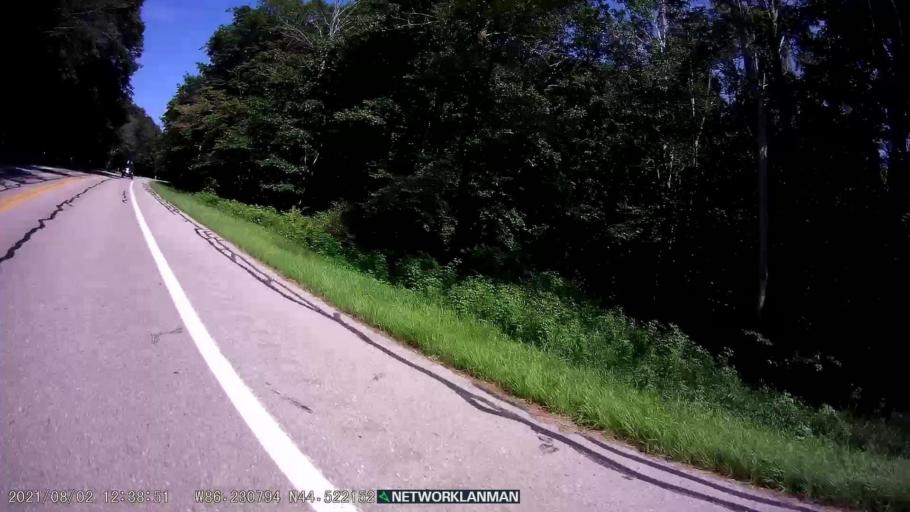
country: US
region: Michigan
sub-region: Benzie County
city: Frankfort
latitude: 44.5224
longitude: -86.2306
